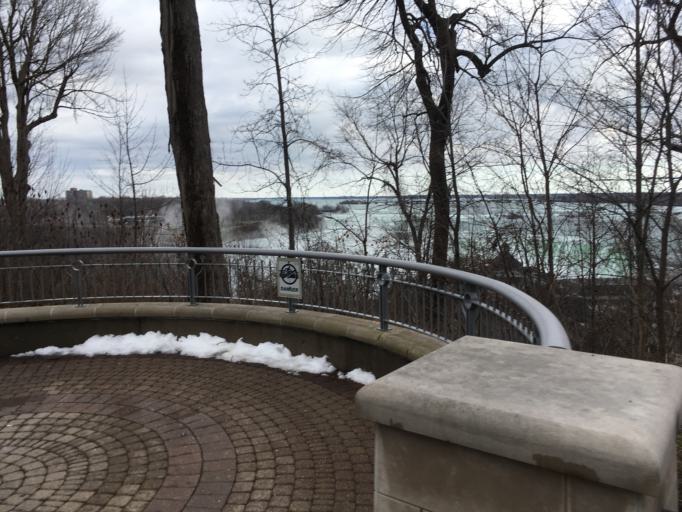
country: CA
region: Ontario
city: Niagara Falls
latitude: 43.0801
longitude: -79.0808
